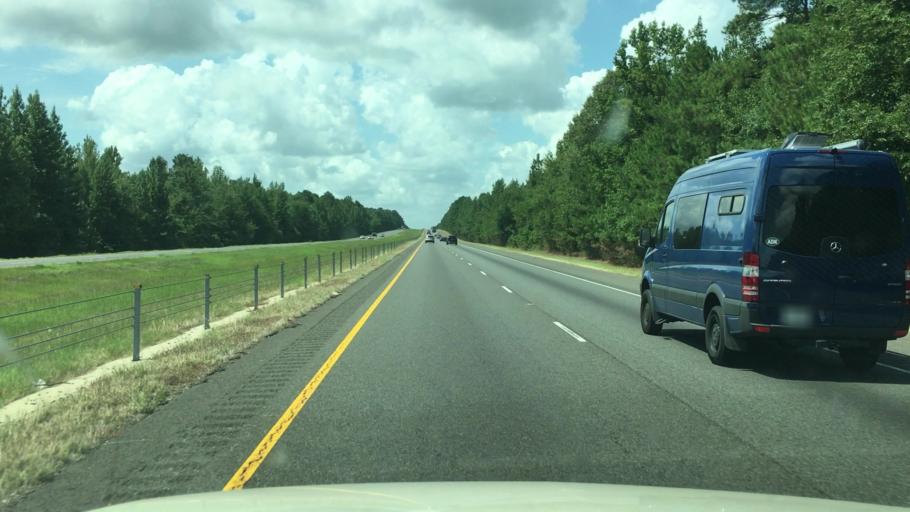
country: US
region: Arkansas
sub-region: Clark County
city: Arkadelphia
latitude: 34.0532
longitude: -93.1327
